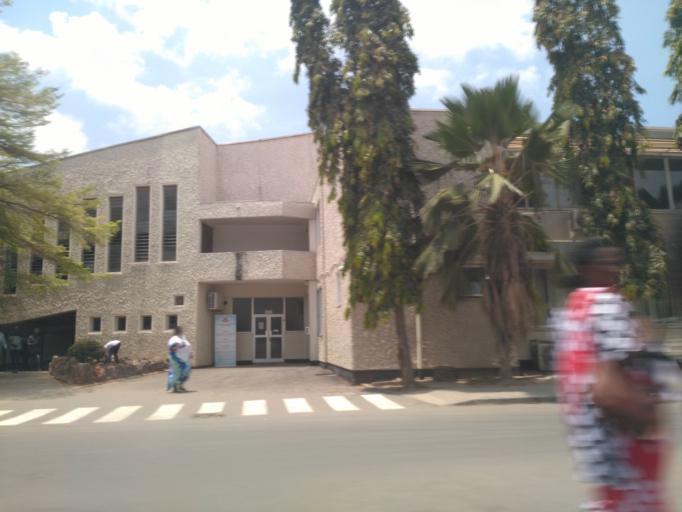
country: TZ
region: Dar es Salaam
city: Dar es Salaam
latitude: -6.8042
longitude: 39.2732
